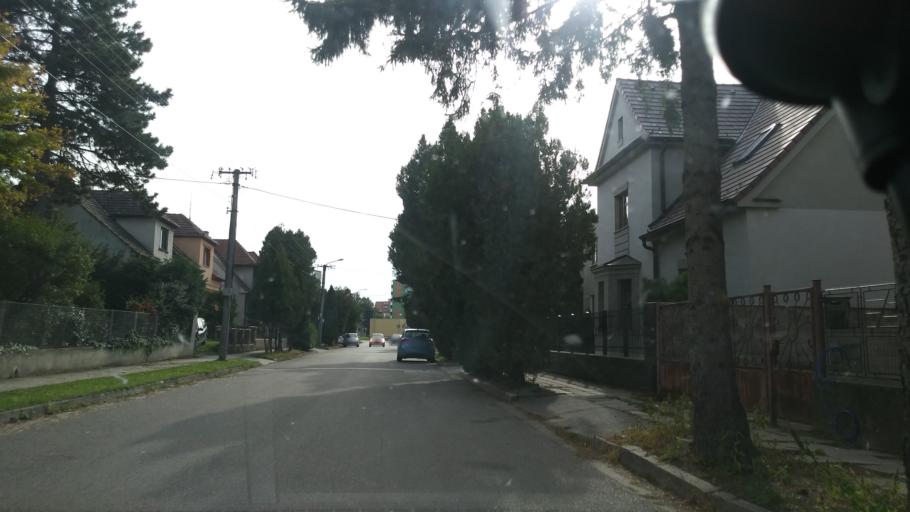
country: SK
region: Trnavsky
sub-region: Okres Skalica
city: Skalica
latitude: 48.8403
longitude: 17.2317
